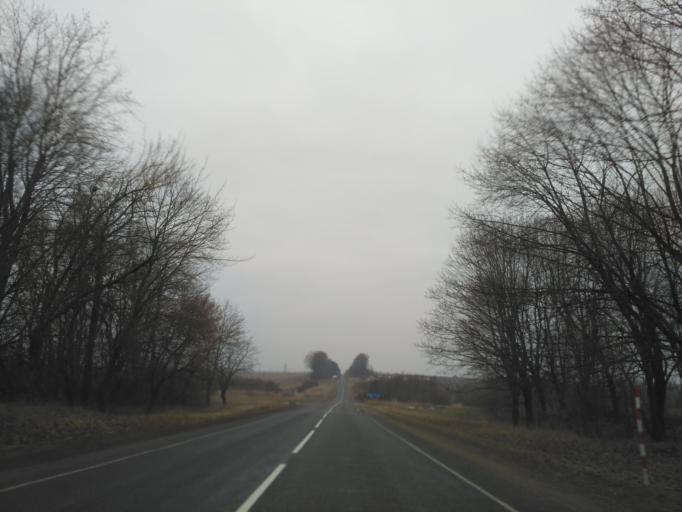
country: BY
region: Minsk
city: Snow
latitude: 53.2542
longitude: 26.2901
